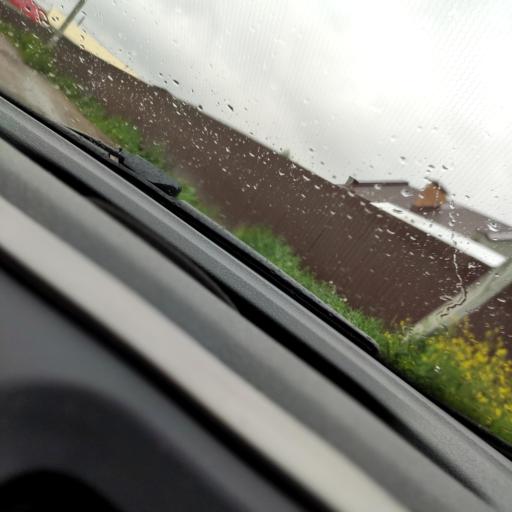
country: RU
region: Samara
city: Tol'yatti
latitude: 53.5082
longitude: 49.2439
